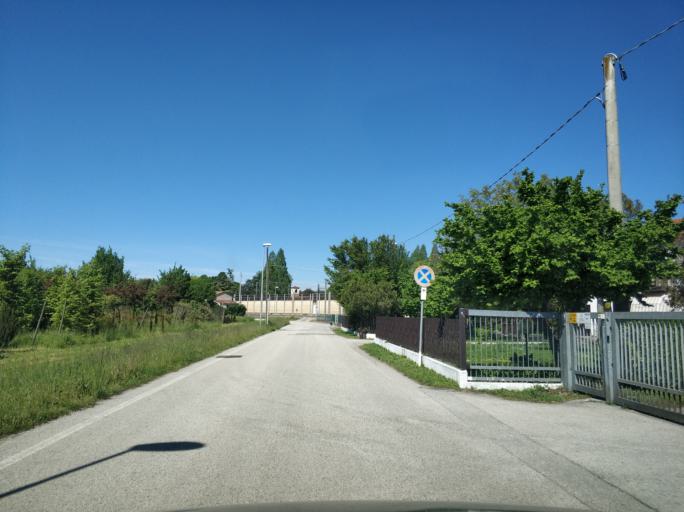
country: IT
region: Veneto
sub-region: Provincia di Venezia
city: Pianiga
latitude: 45.4405
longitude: 12.0108
